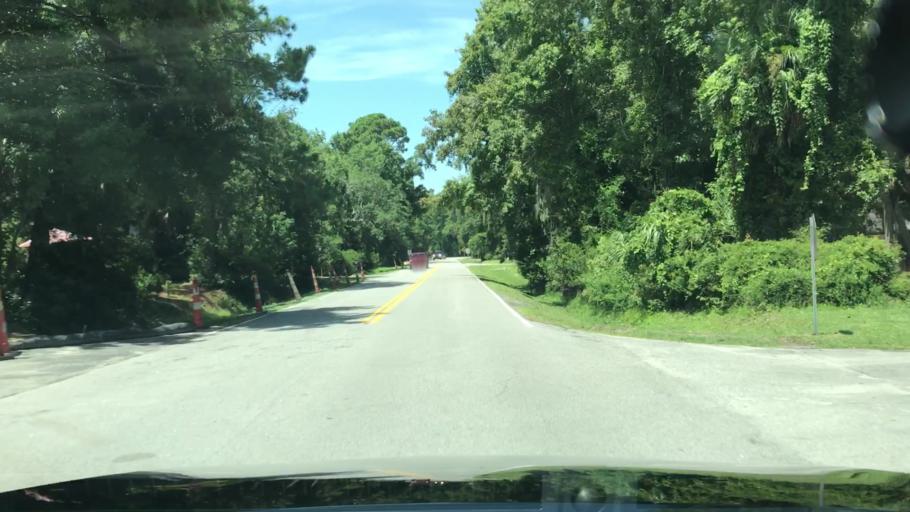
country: US
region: South Carolina
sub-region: Beaufort County
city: Hilton Head Island
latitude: 32.1354
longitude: -80.7682
